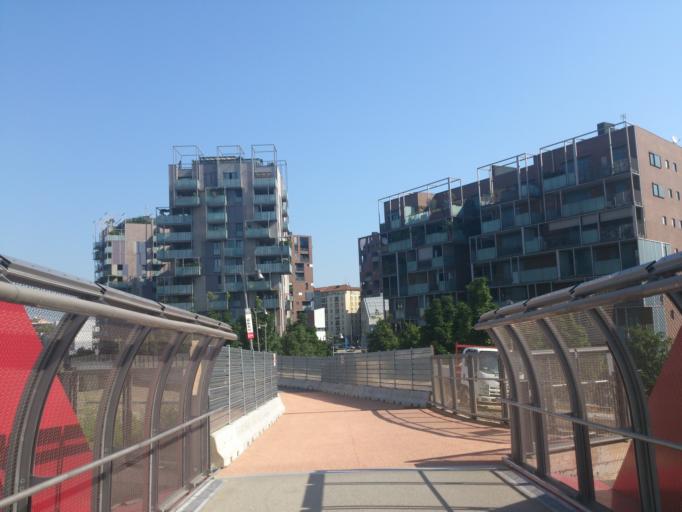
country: IT
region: Lombardy
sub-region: Citta metropolitana di Milano
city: Novate Milanese
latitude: 45.4877
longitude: 9.1476
